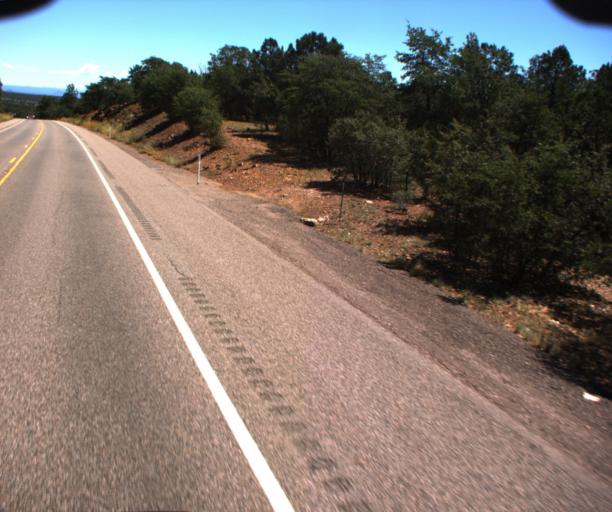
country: US
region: Arizona
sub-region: Navajo County
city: Cibecue
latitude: 33.6993
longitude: -110.5473
